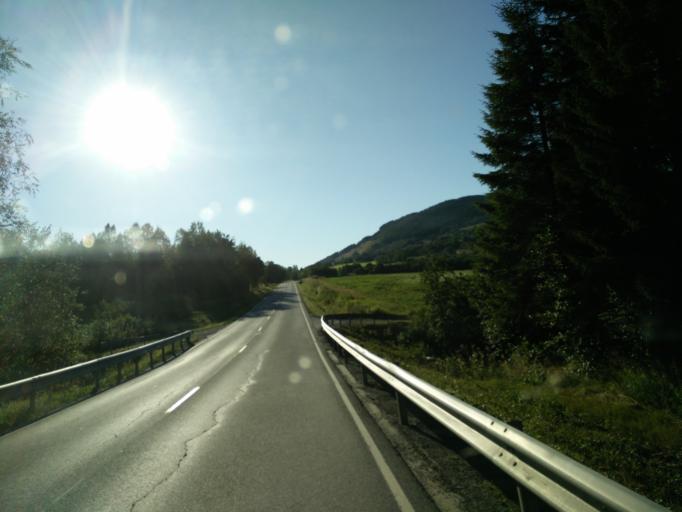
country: NO
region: More og Romsdal
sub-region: Halsa
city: Liaboen
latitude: 63.0720
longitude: 8.2781
